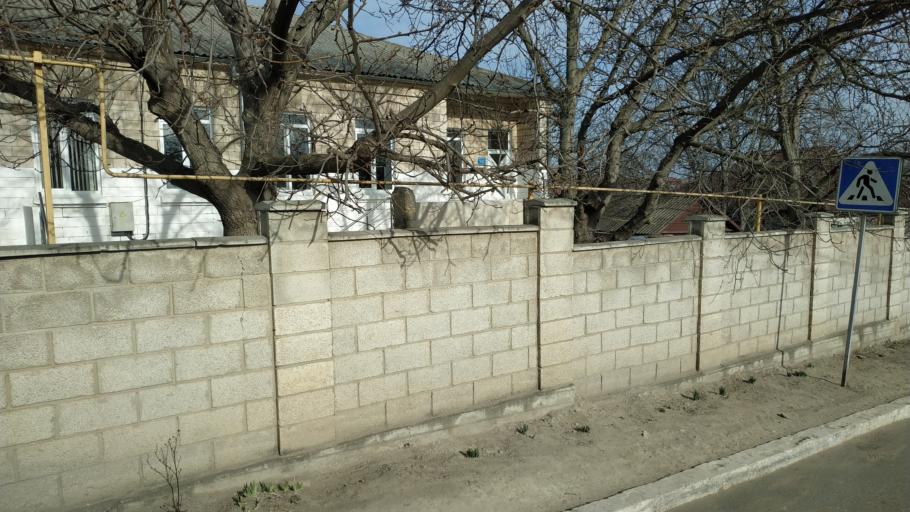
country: MD
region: Chisinau
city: Vatra
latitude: 47.0755
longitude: 28.6894
